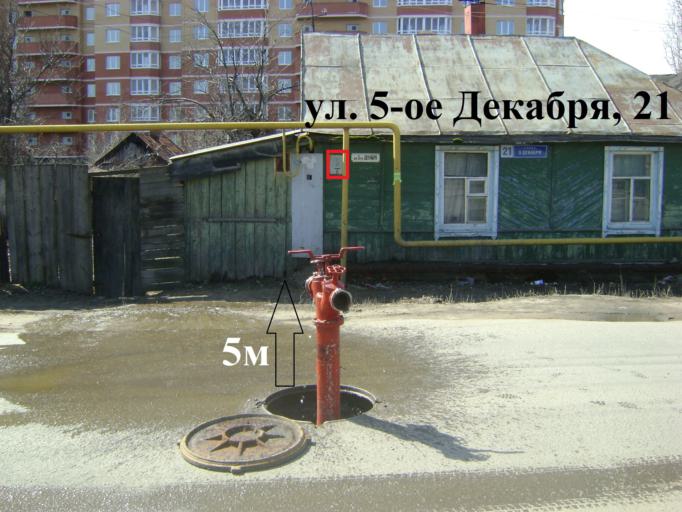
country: RU
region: Voronezj
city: Voronezh
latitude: 51.6495
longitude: 39.1904
